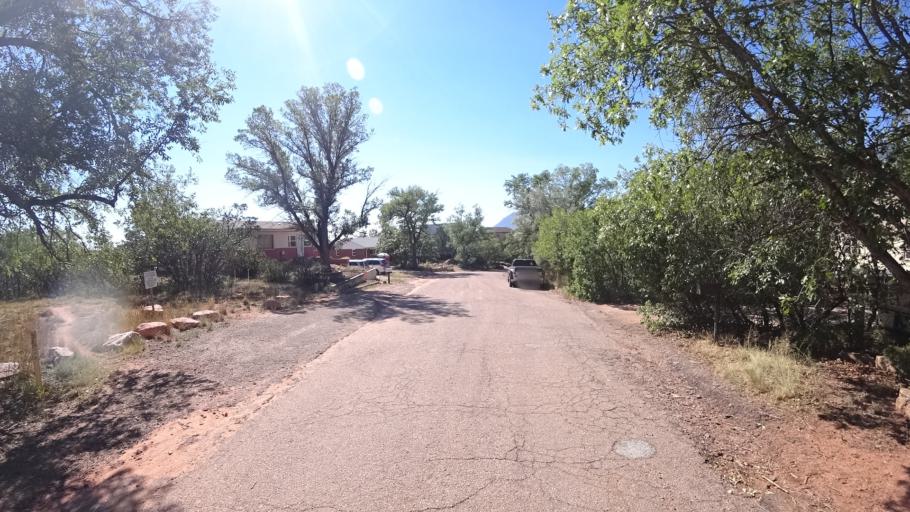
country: US
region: Colorado
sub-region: El Paso County
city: Manitou Springs
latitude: 38.8606
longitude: -104.8785
